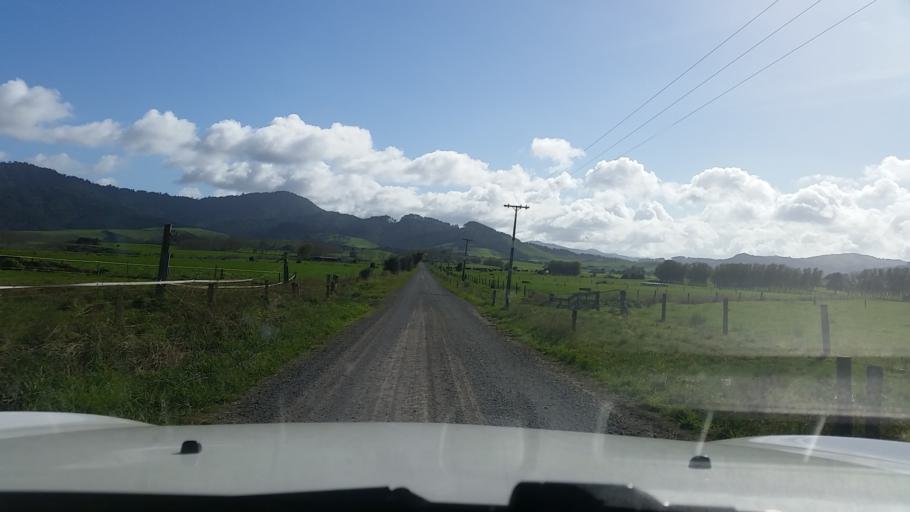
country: NZ
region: Waikato
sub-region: Hauraki District
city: Ngatea
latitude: -37.5144
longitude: 175.4100
